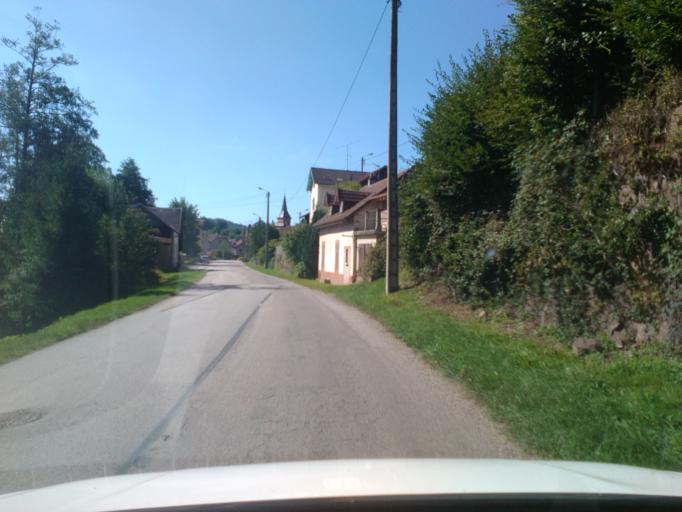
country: FR
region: Lorraine
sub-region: Departement des Vosges
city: Senones
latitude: 48.4092
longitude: 6.9962
